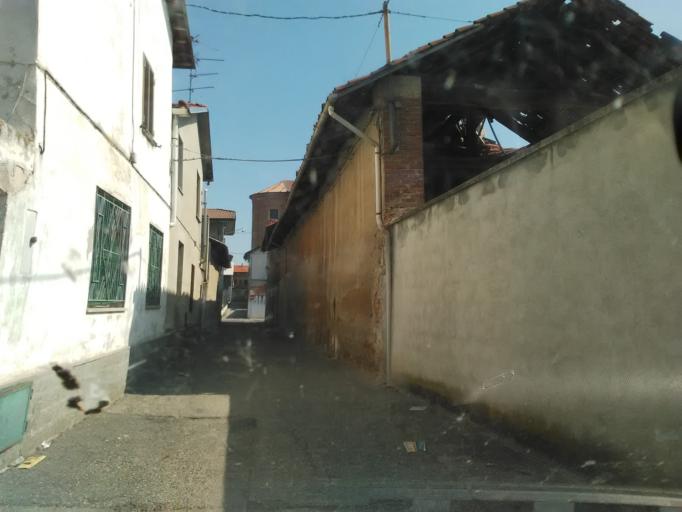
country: IT
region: Piedmont
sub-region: Provincia di Vercelli
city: Livorno Ferraris
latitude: 45.2807
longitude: 8.0781
